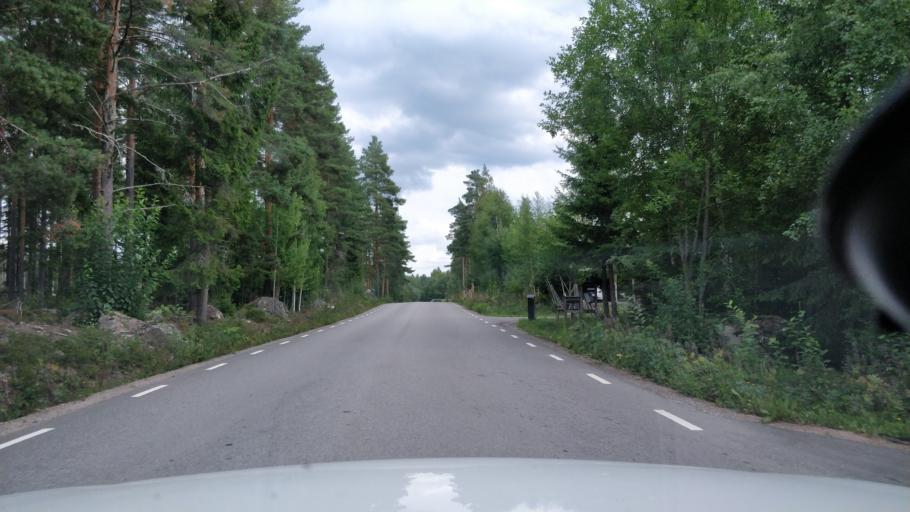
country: SE
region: Dalarna
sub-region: Faluns Kommun
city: Bjursas
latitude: 60.7493
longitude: 15.4761
